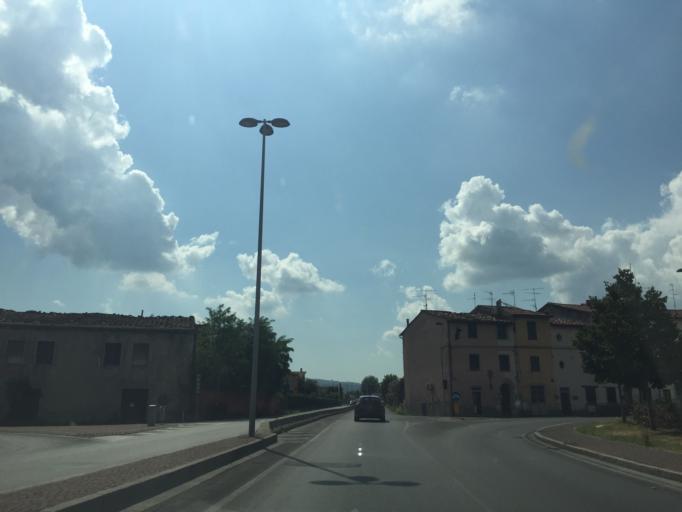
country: IT
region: Tuscany
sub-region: Provincia di Pistoia
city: Pistoia
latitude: 43.9232
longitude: 10.9253
